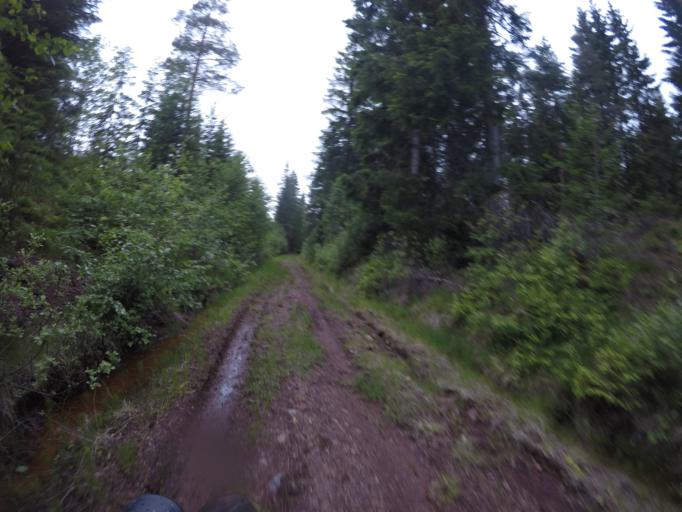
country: SE
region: OErebro
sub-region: Hallefors Kommun
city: Haellefors
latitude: 60.0267
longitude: 14.5620
